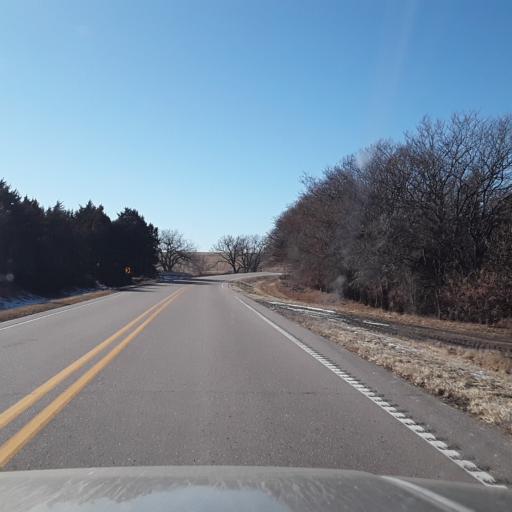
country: US
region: Nebraska
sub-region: Frontier County
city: Stockville
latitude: 40.7022
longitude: -100.2525
